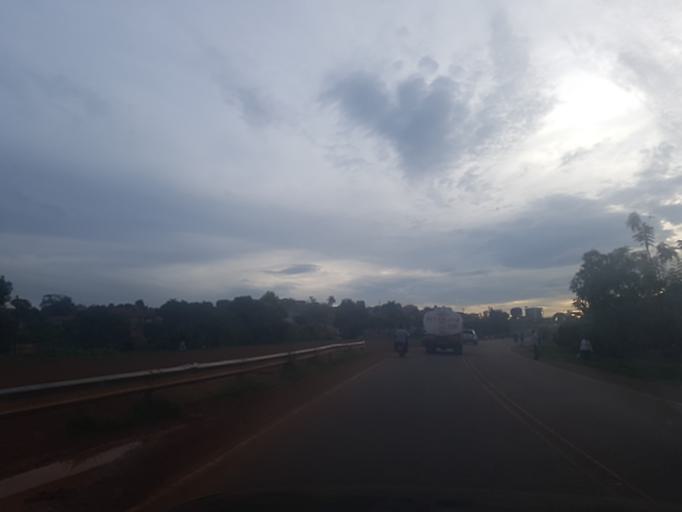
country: UG
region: Central Region
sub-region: Wakiso District
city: Kireka
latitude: 0.3657
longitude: 32.6103
